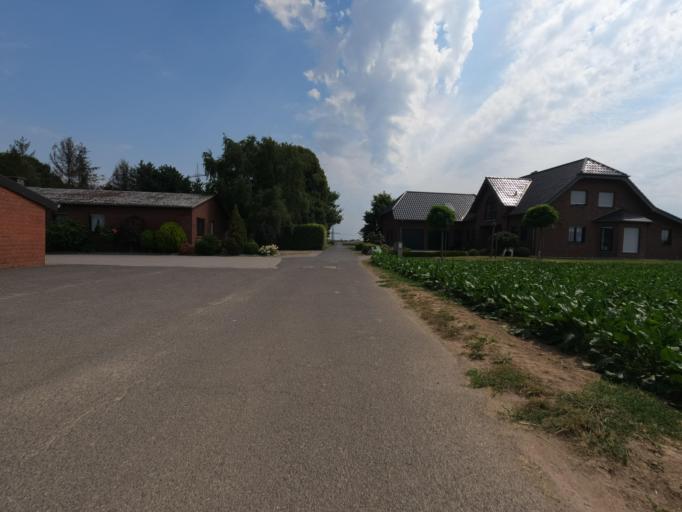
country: DE
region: North Rhine-Westphalia
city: Baesweiler
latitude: 50.9143
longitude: 6.2085
